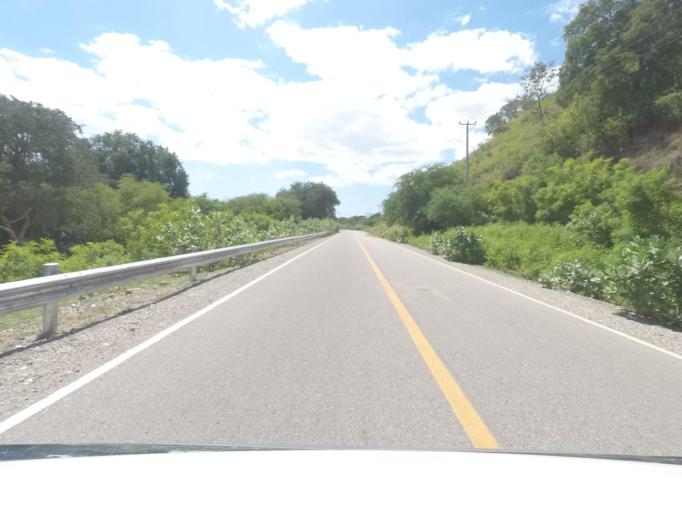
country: TL
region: Lautem
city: Lospalos
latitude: -8.3710
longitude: 126.8941
